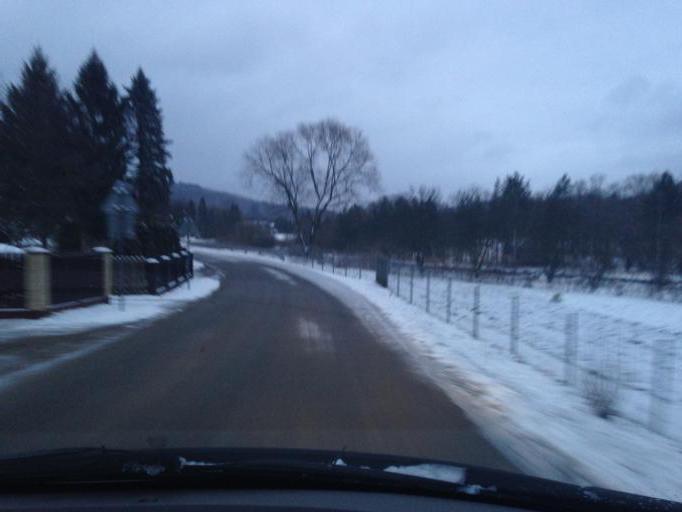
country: PL
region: Subcarpathian Voivodeship
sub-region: Powiat jasielski
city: Krempna
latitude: 49.5101
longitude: 21.5035
